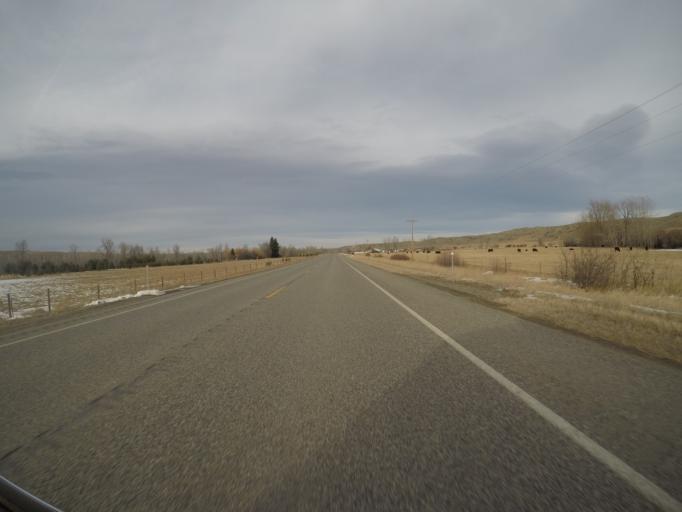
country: US
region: Montana
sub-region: Stillwater County
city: Absarokee
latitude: 45.4535
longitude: -109.4489
